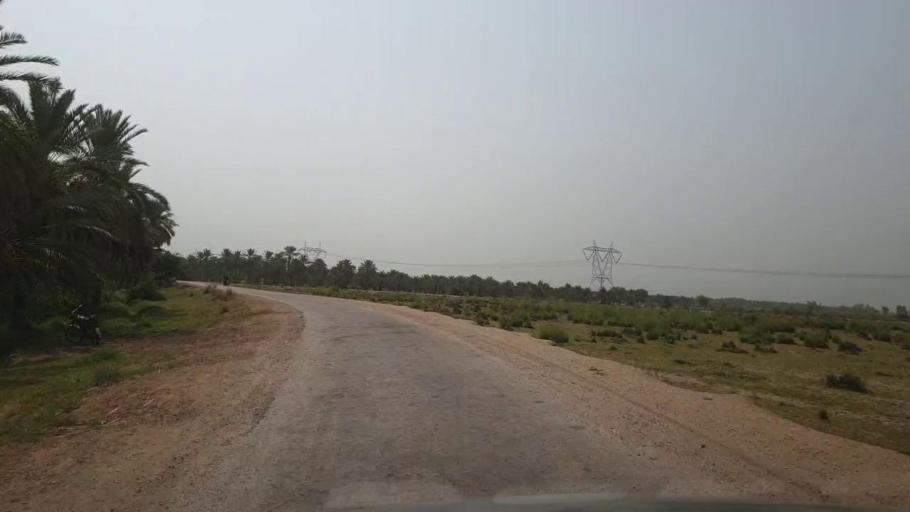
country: PK
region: Sindh
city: Gambat
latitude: 27.4167
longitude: 68.5486
